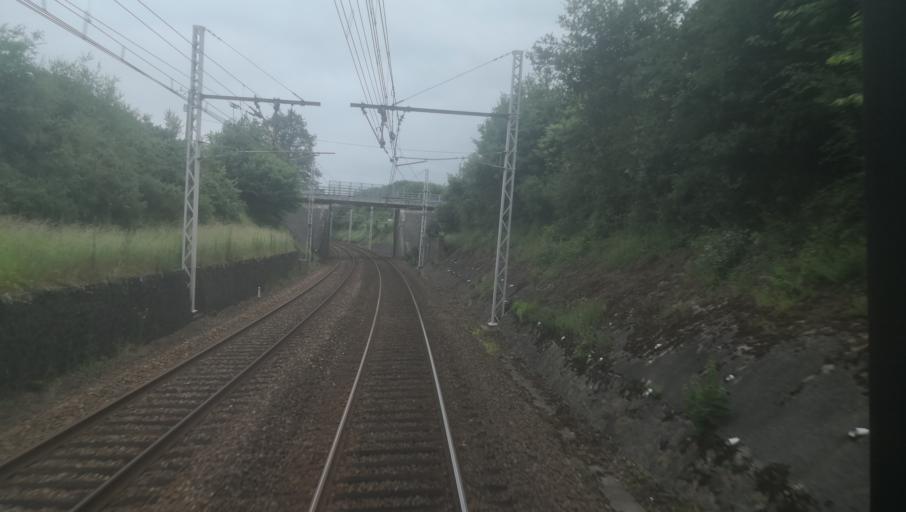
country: FR
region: Centre
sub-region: Departement de l'Indre
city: Le Pechereau
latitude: 46.5475
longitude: 1.5420
